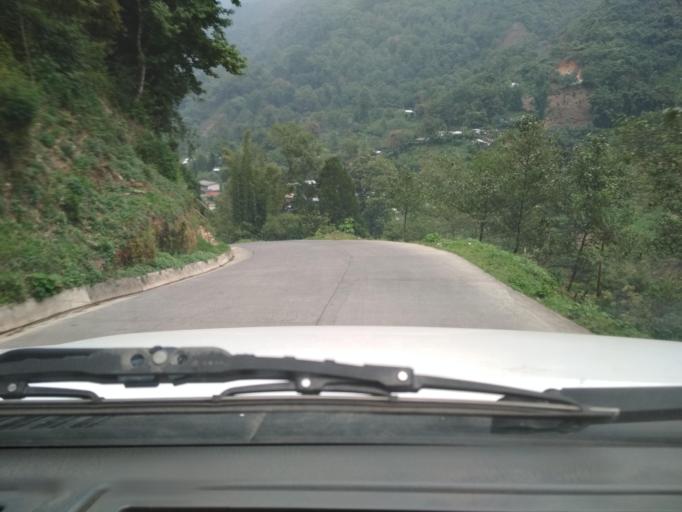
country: MX
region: Veracruz
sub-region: La Perla
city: Barrio de San Miguel
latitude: 18.9342
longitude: -97.1263
